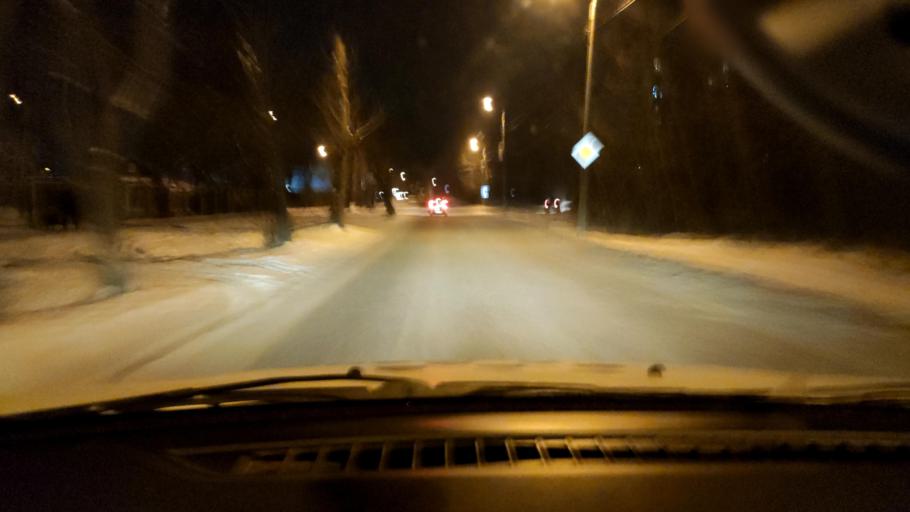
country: RU
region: Perm
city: Overyata
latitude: 58.0119
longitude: 55.9595
